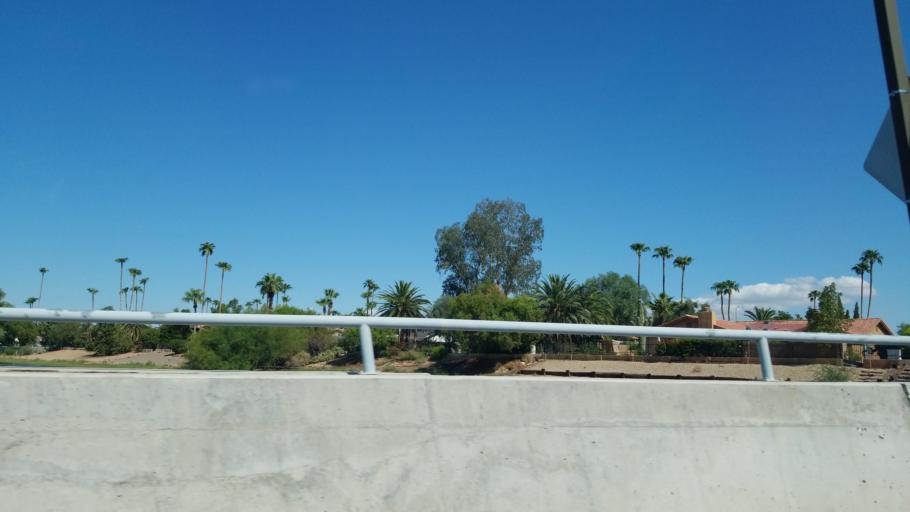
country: US
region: Arizona
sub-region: Maricopa County
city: Paradise Valley
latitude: 33.5385
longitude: -111.9135
